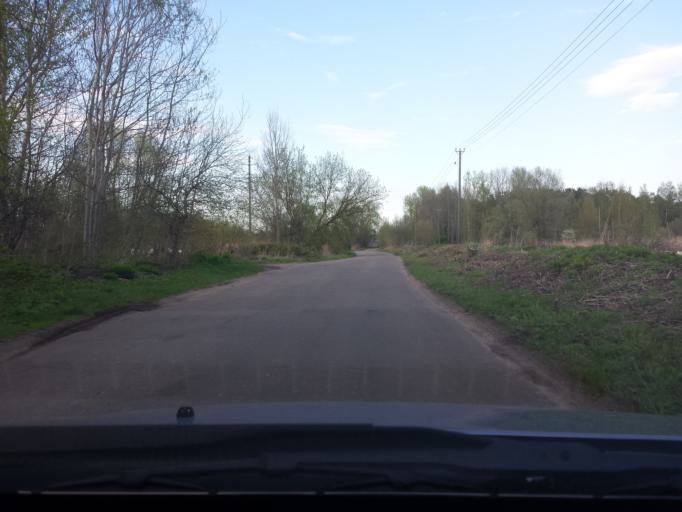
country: LV
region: Riga
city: Jaunciems
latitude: 56.9944
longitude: 24.2165
